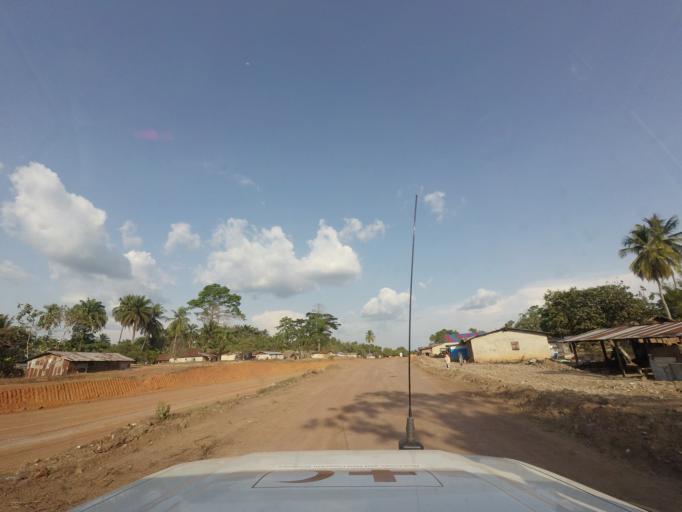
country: LR
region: Bong
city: Gbarnga
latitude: 7.0435
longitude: -9.5189
